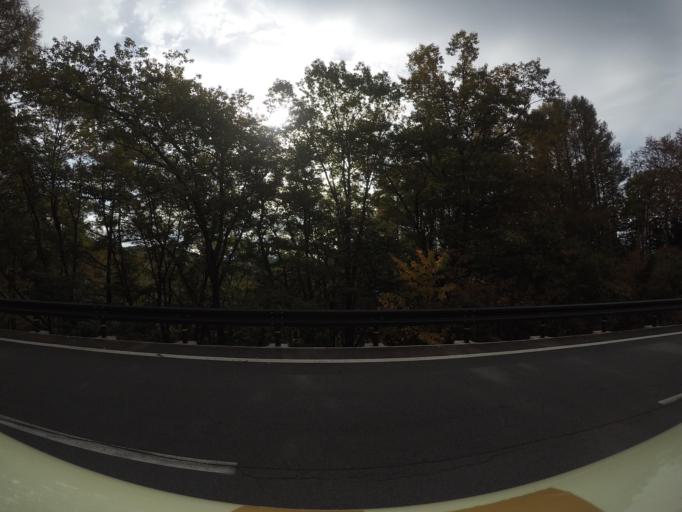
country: JP
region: Gifu
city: Takayama
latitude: 35.9378
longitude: 137.5819
